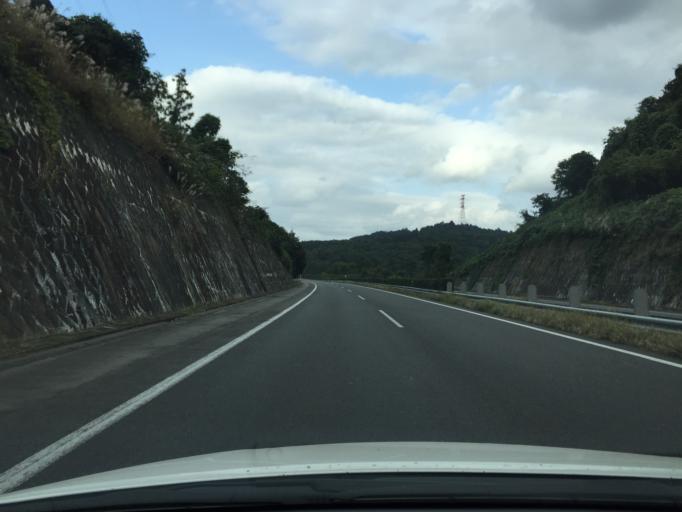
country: JP
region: Ibaraki
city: Kitaibaraki
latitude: 36.9323
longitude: 140.7682
